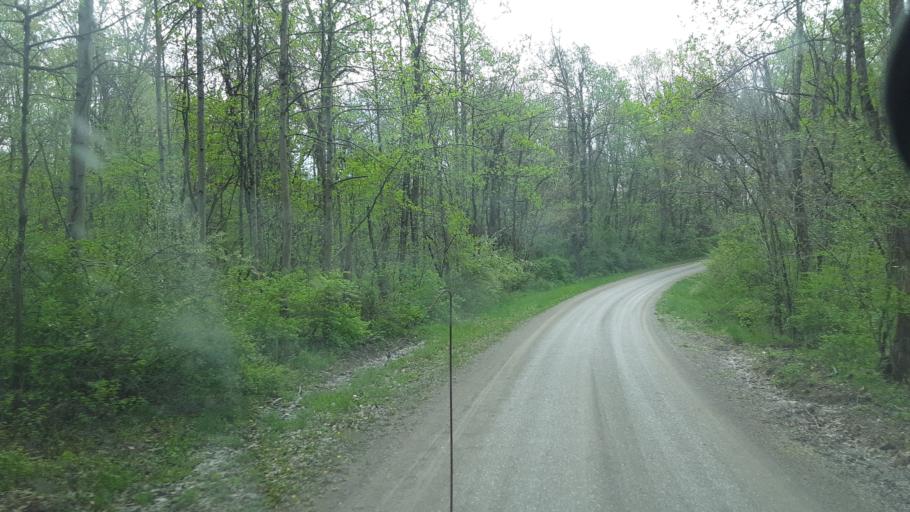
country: US
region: Ohio
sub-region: Noble County
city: Caldwell
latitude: 39.7688
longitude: -81.6161
